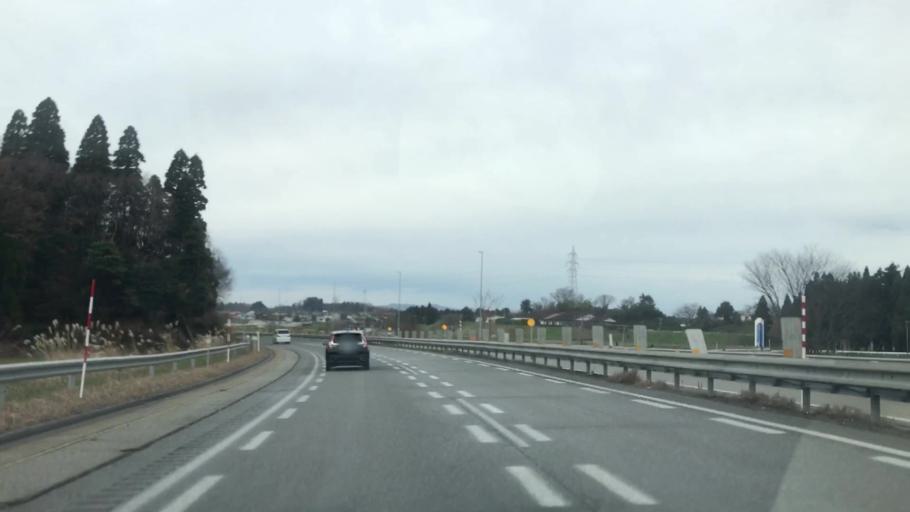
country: JP
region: Toyama
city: Kuragaki-kosugi
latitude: 36.6910
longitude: 137.0959
